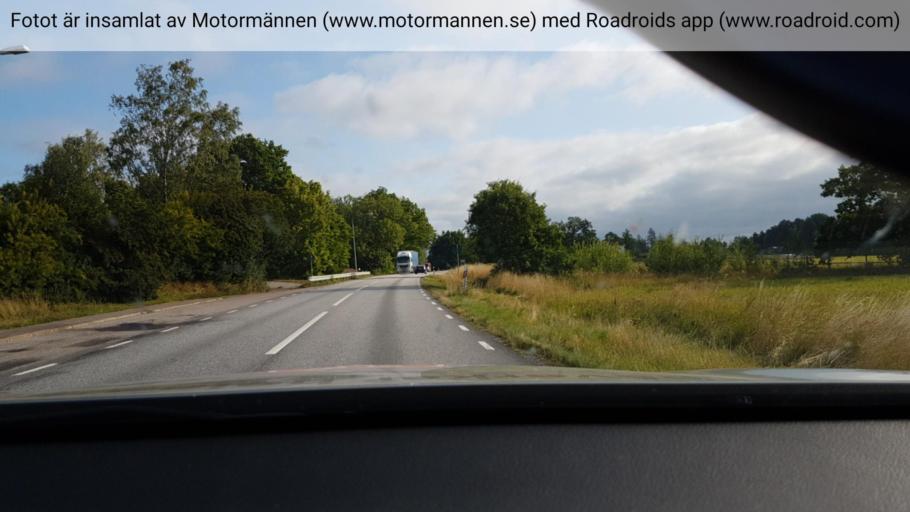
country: SE
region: Stockholm
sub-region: Norrtalje Kommun
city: Rimbo
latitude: 59.6835
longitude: 18.3662
